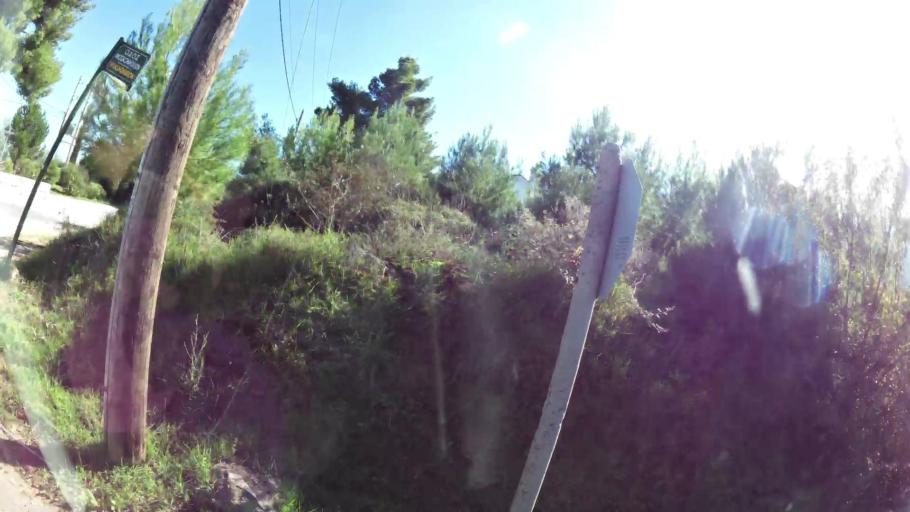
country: GR
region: Attica
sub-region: Nomarchia Anatolikis Attikis
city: Dionysos
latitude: 38.0969
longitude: 23.8891
